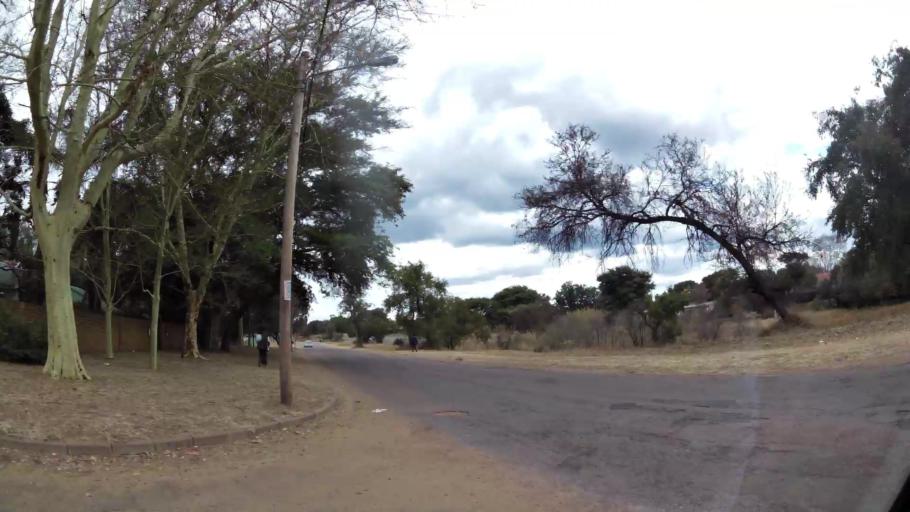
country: ZA
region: Limpopo
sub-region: Waterberg District Municipality
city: Modimolle
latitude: -24.7011
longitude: 28.4122
